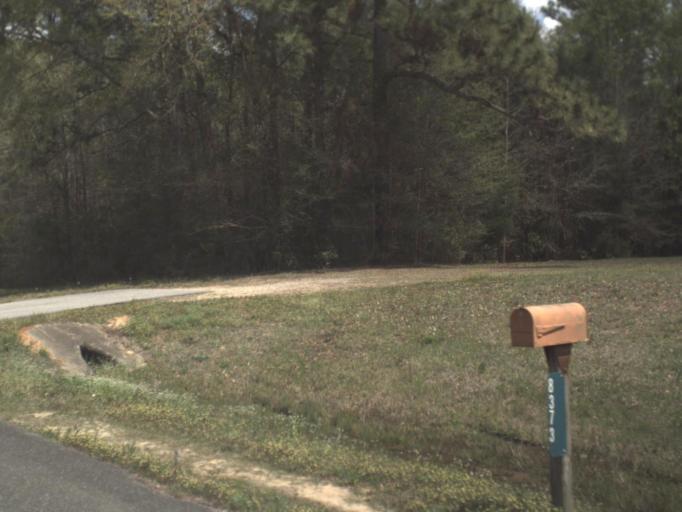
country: US
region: Florida
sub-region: Okaloosa County
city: Crestview
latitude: 30.9821
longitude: -86.6301
